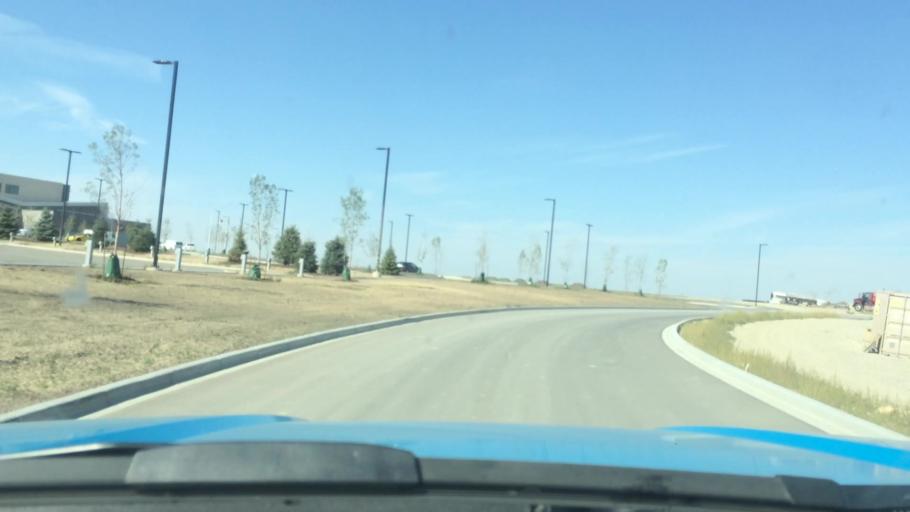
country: CA
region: Alberta
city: Airdrie
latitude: 51.2172
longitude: -113.9379
